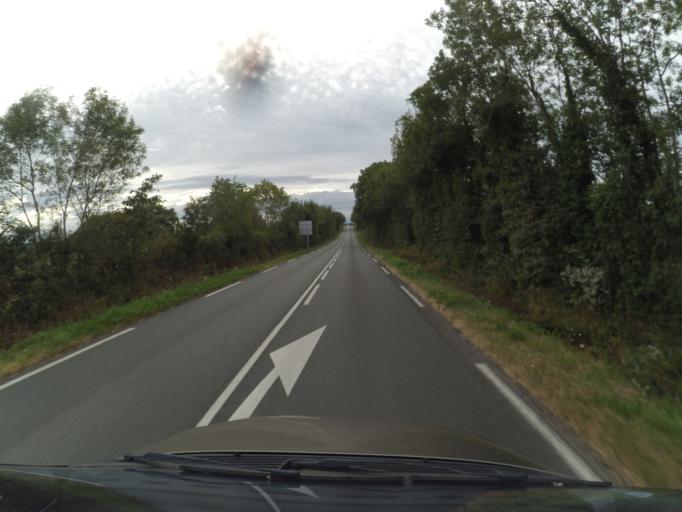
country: FR
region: Pays de la Loire
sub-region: Departement de la Vendee
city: Saint-Aubin-des-Ormeaux
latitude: 47.0152
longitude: -0.9980
